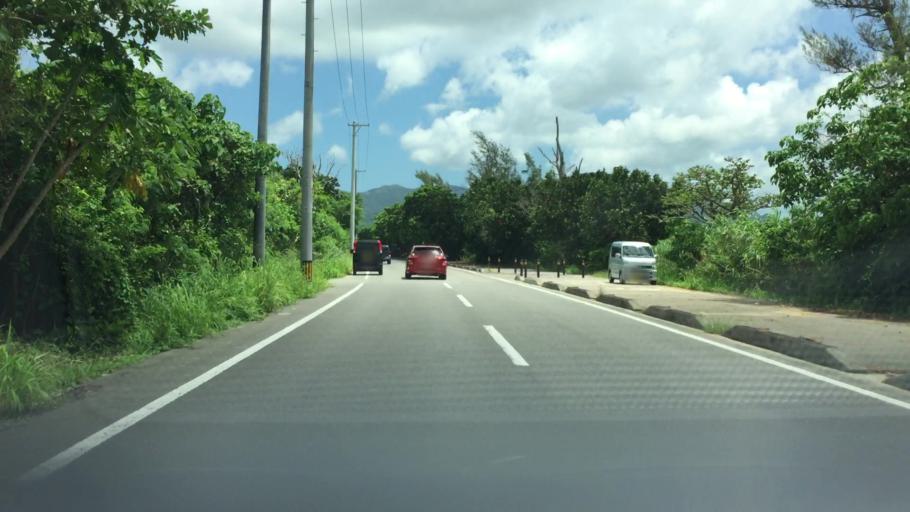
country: JP
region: Okinawa
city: Ishigaki
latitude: 24.3864
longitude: 124.1388
